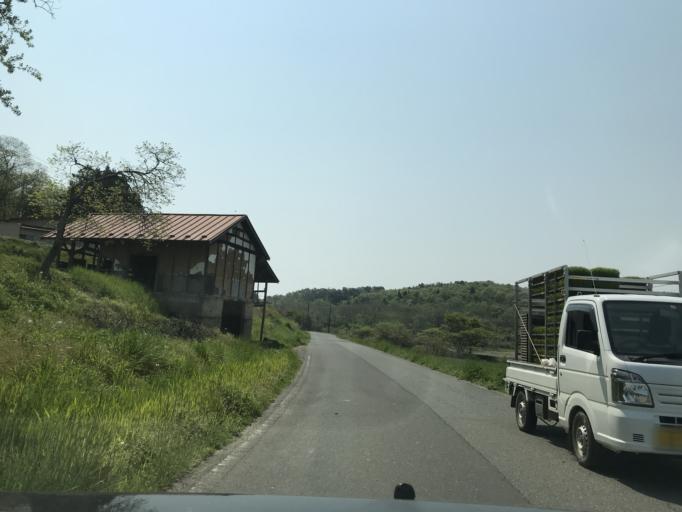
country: JP
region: Iwate
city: Ichinoseki
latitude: 38.8391
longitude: 141.0723
